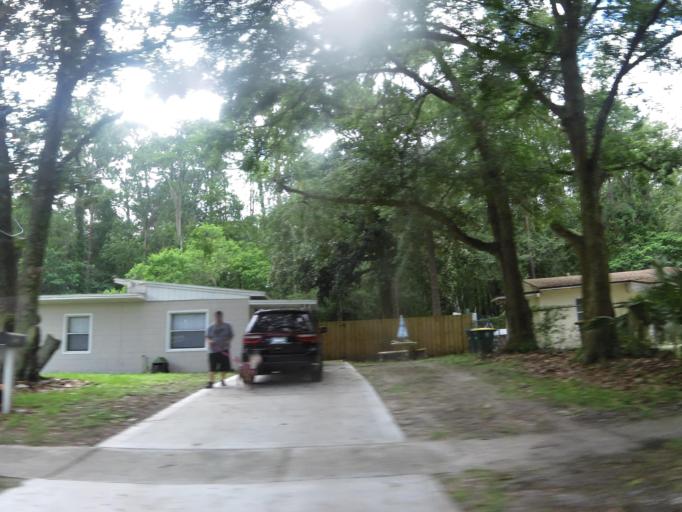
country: US
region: Florida
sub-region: Duval County
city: Jacksonville
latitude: 30.2813
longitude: -81.5551
